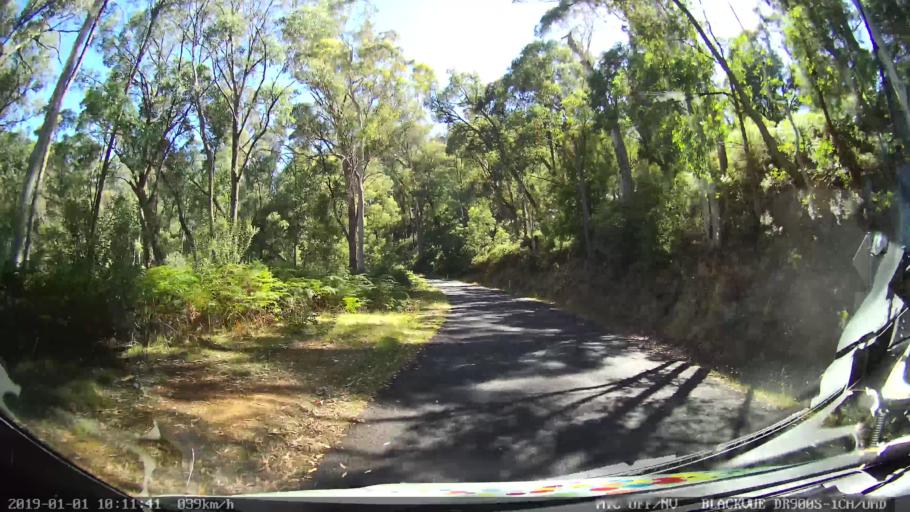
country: AU
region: New South Wales
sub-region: Snowy River
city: Jindabyne
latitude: -36.1357
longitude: 148.1558
